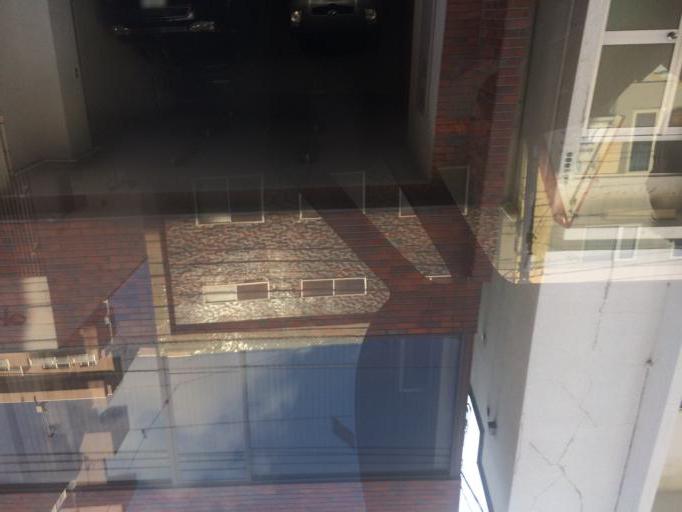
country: JP
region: Hokkaido
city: Sapporo
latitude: 43.0419
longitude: 141.3506
